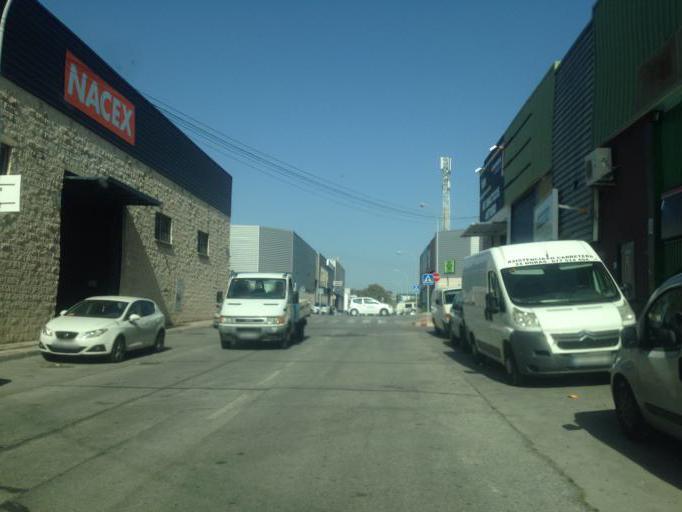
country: ES
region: Andalusia
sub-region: Provincia de Malaga
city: Malaga
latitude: 36.7097
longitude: -4.4684
